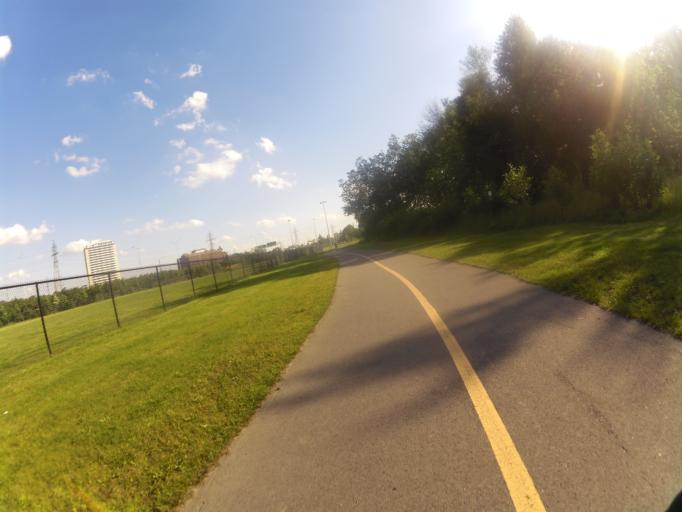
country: CA
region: Ontario
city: Ottawa
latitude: 45.3887
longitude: -75.7366
